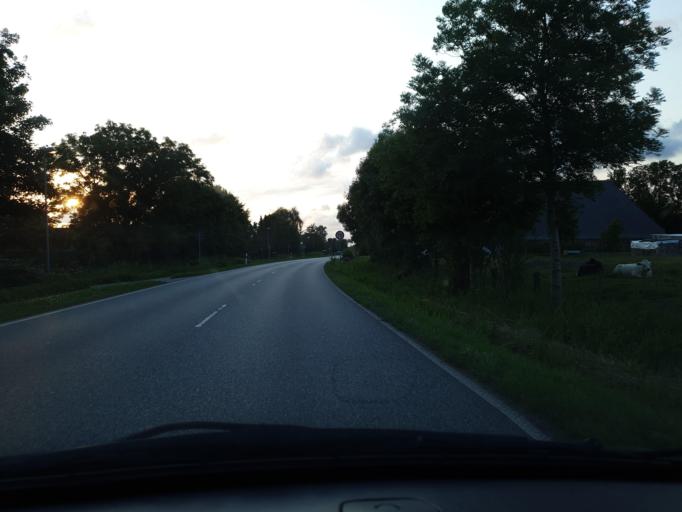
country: DE
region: Schleswig-Holstein
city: Diekhusen-Fahrstedt
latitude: 53.9353
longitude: 9.0306
